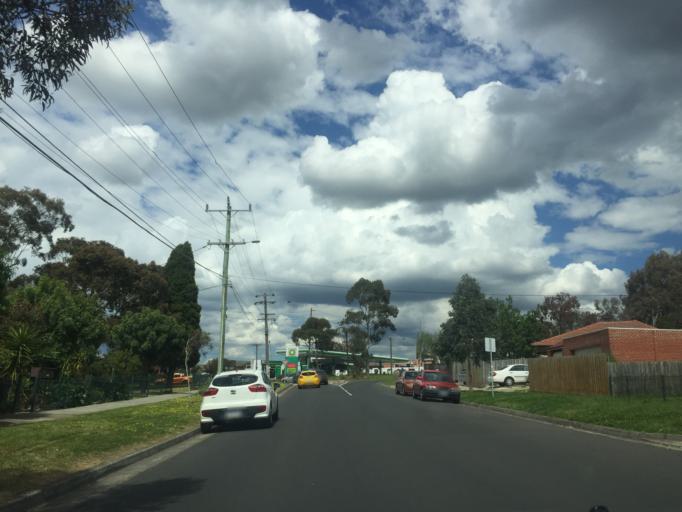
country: AU
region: Victoria
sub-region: Darebin
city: Kingsbury
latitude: -37.7176
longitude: 145.0207
